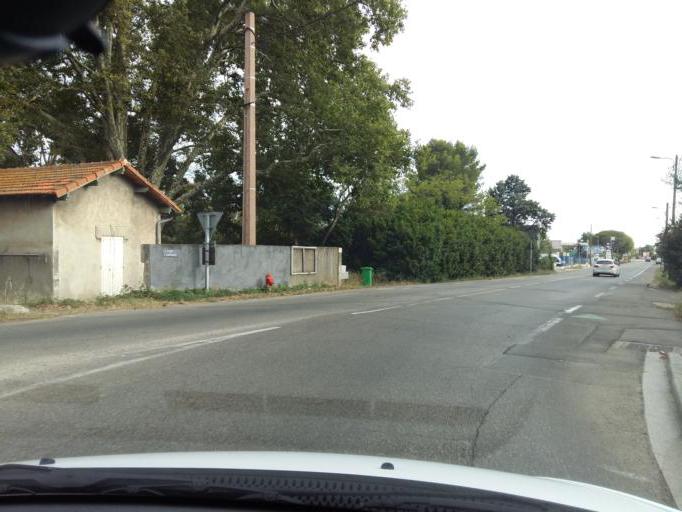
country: FR
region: Provence-Alpes-Cote d'Azur
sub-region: Departement du Vaucluse
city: Le Pontet
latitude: 43.9450
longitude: 4.8545
